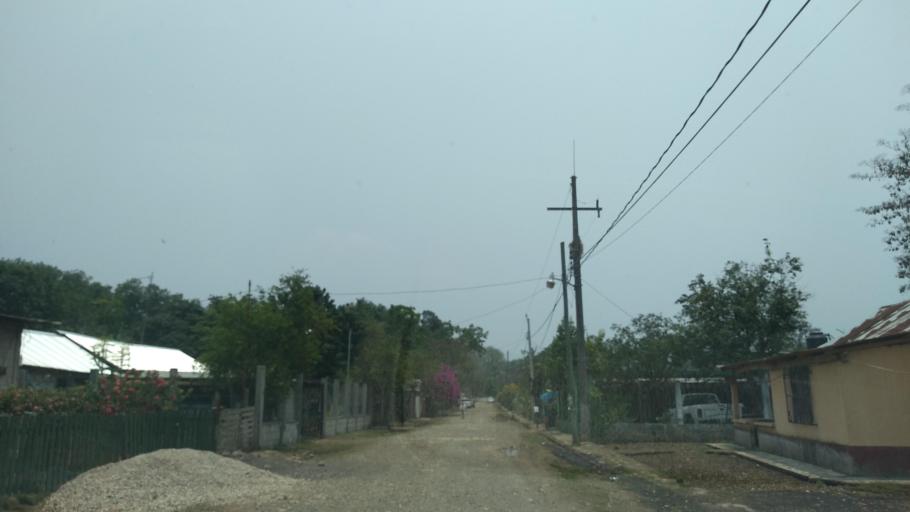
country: MX
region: Veracruz
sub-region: Tezonapa
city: Laguna Chica (Pueblo Nuevo)
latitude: 18.5130
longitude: -96.7656
